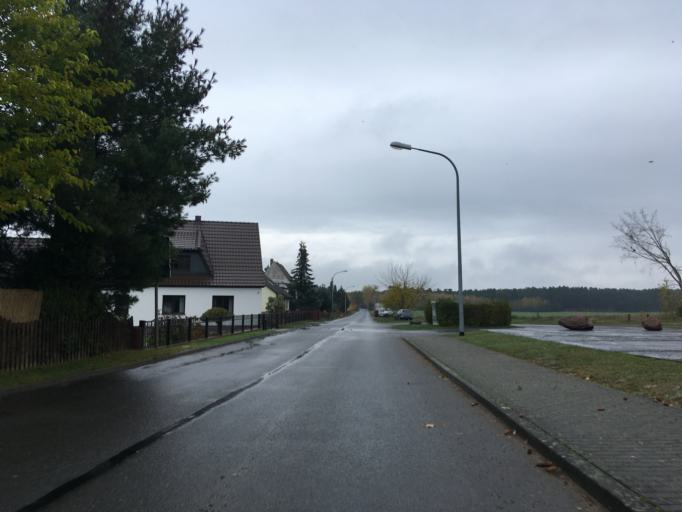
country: DE
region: Brandenburg
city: Friedland
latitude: 52.0433
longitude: 14.1830
